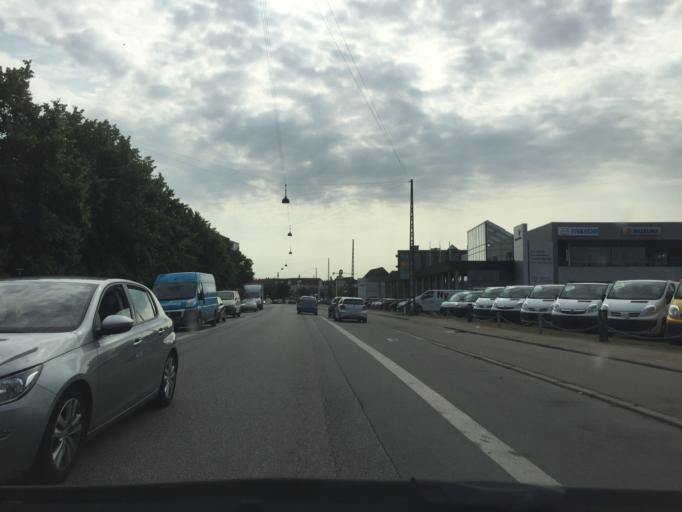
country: DK
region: Capital Region
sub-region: Frederiksberg Kommune
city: Frederiksberg
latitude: 55.7065
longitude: 12.5473
